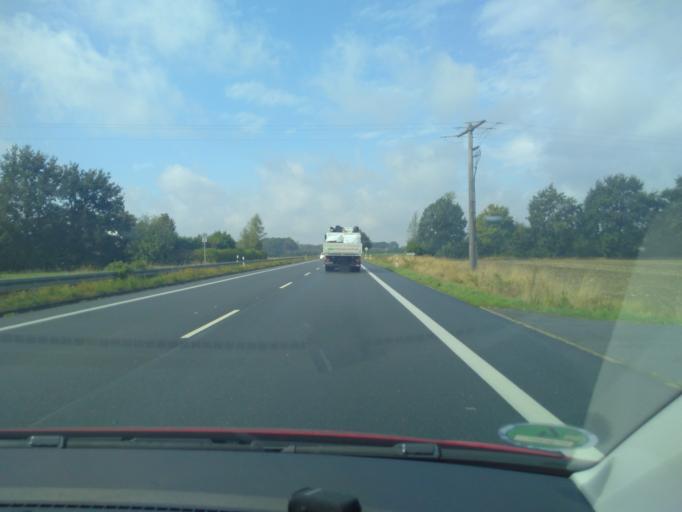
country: DE
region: North Rhine-Westphalia
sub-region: Regierungsbezirk Munster
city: Sassenberg
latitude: 51.9444
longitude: 8.0514
